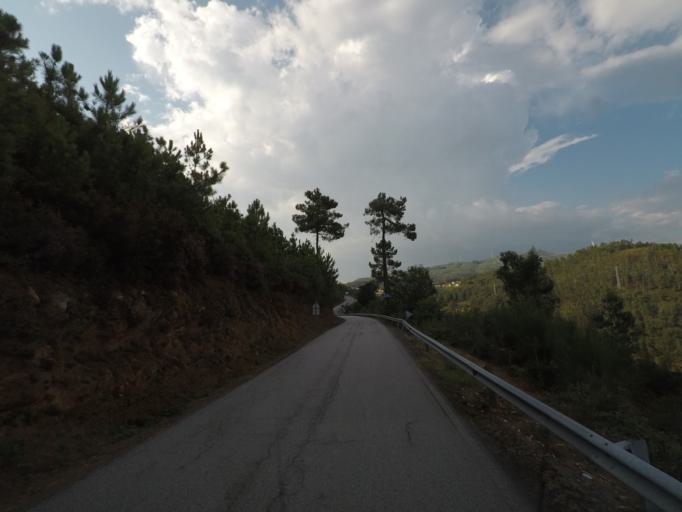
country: PT
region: Porto
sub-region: Baiao
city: Valadares
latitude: 41.1811
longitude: -7.9364
